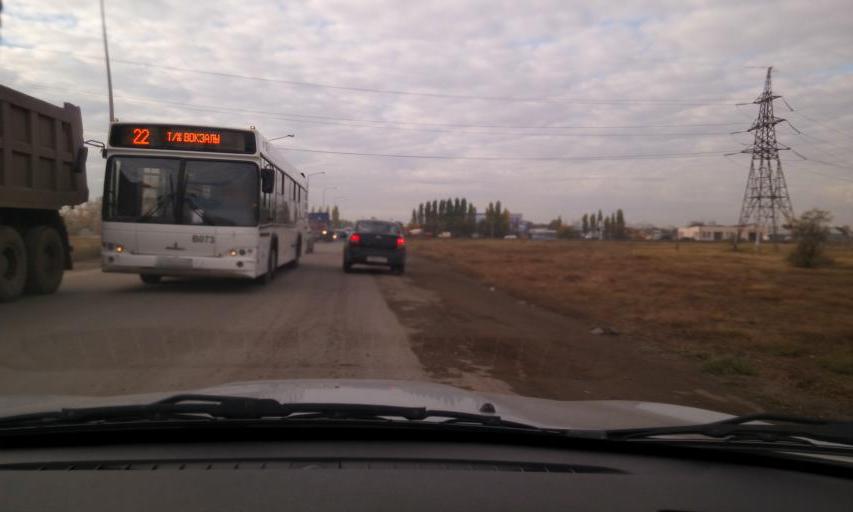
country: KZ
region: Astana Qalasy
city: Astana
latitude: 51.1381
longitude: 71.5283
